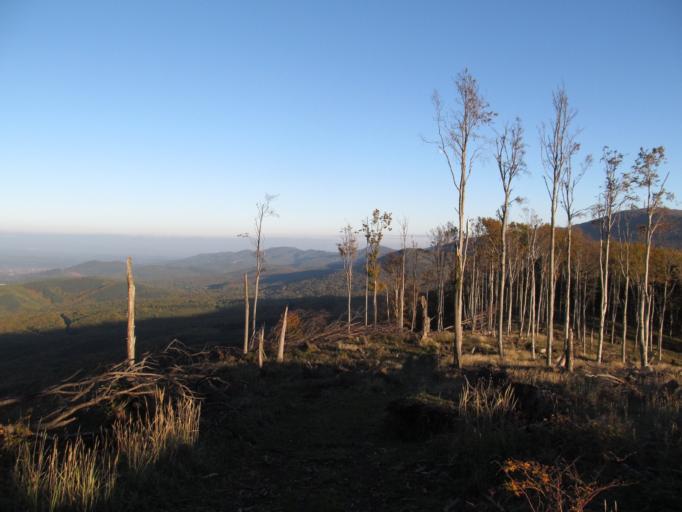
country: HU
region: Heves
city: Paradsasvar
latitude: 47.9030
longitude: 19.9600
